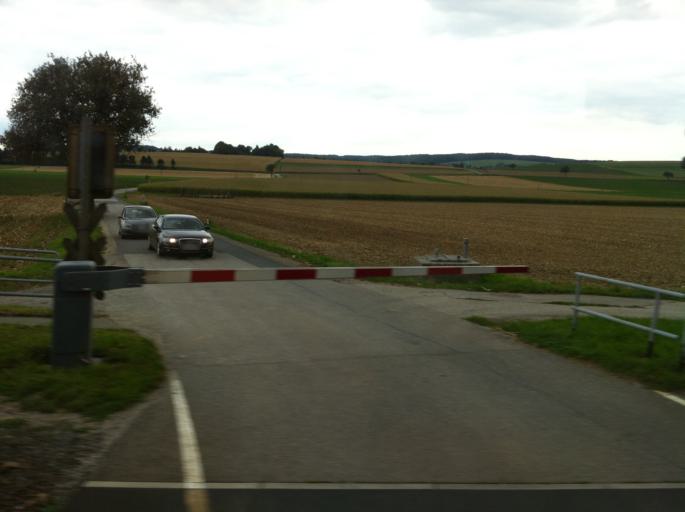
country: AT
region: Lower Austria
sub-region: Politischer Bezirk Sankt Polten
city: Kirchstetten
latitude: 48.1918
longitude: 15.8485
